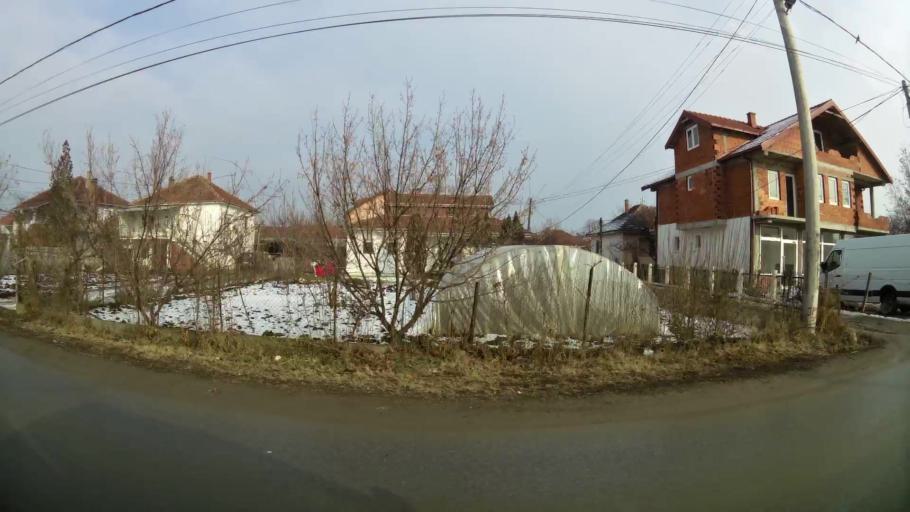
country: MK
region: Ilinden
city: Marino
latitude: 41.9938
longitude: 21.5885
